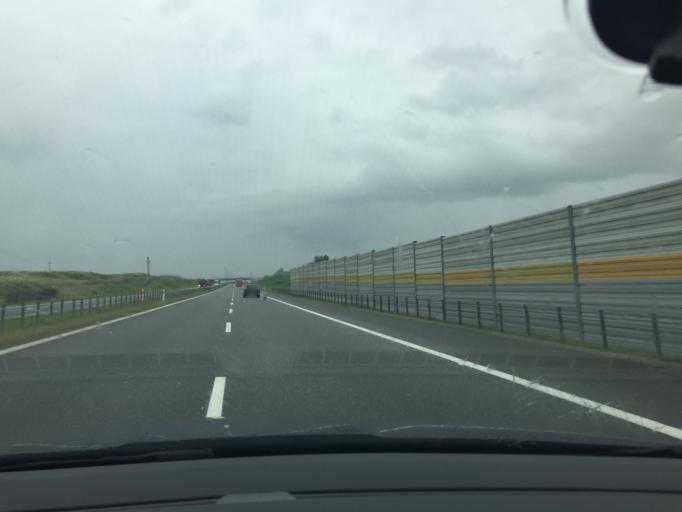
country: PL
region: Kujawsko-Pomorskie
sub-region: Powiat chelminski
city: Lisewo
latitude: 53.3575
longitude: 18.7019
